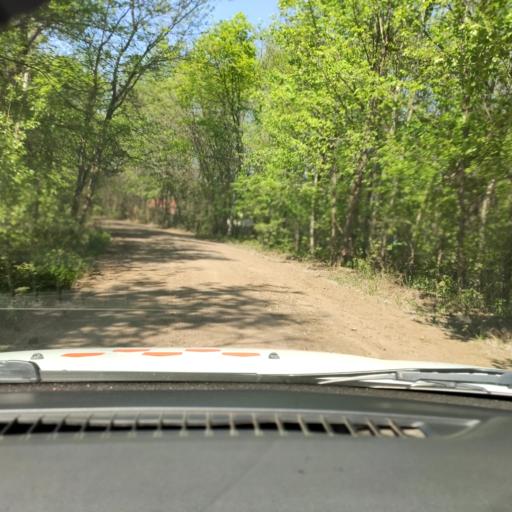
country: RU
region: Bashkortostan
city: Ufa
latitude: 54.6858
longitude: 55.8783
